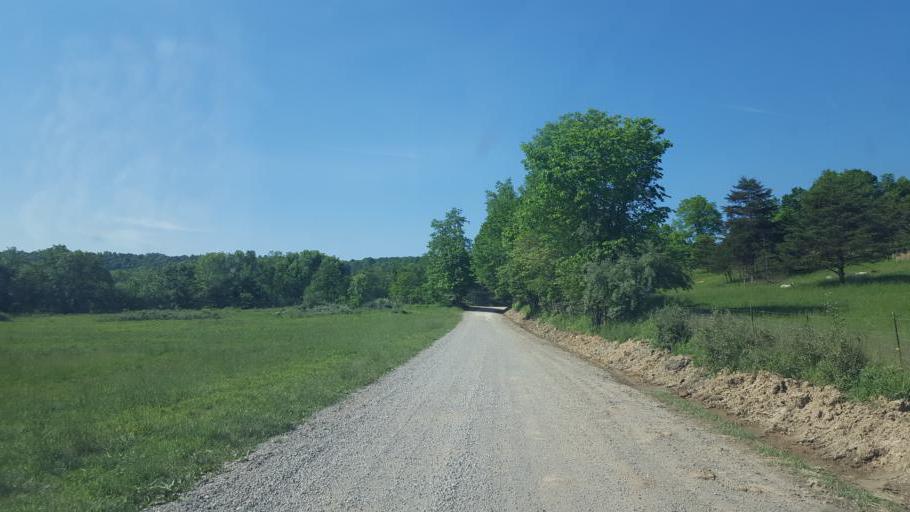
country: US
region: Ohio
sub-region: Jackson County
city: Wellston
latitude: 38.9947
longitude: -82.4179
